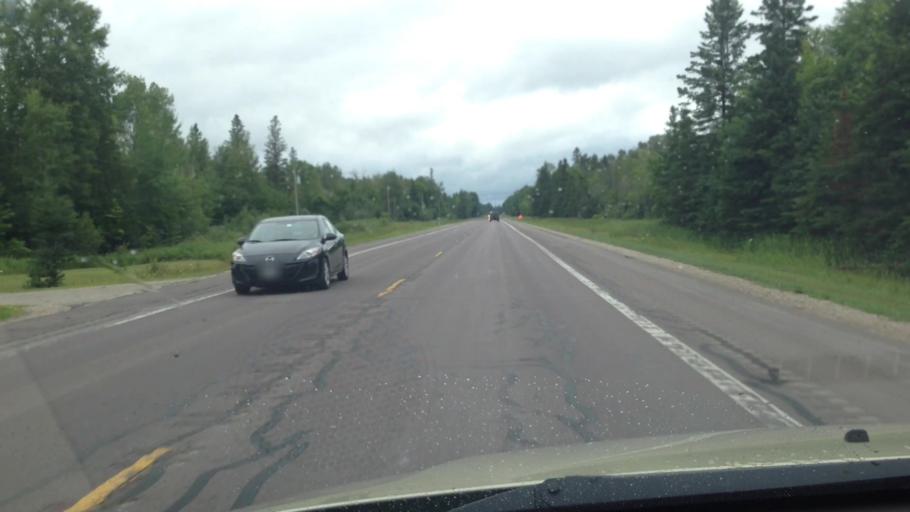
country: US
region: Michigan
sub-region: Schoolcraft County
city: Manistique
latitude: 46.0644
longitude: -85.9584
